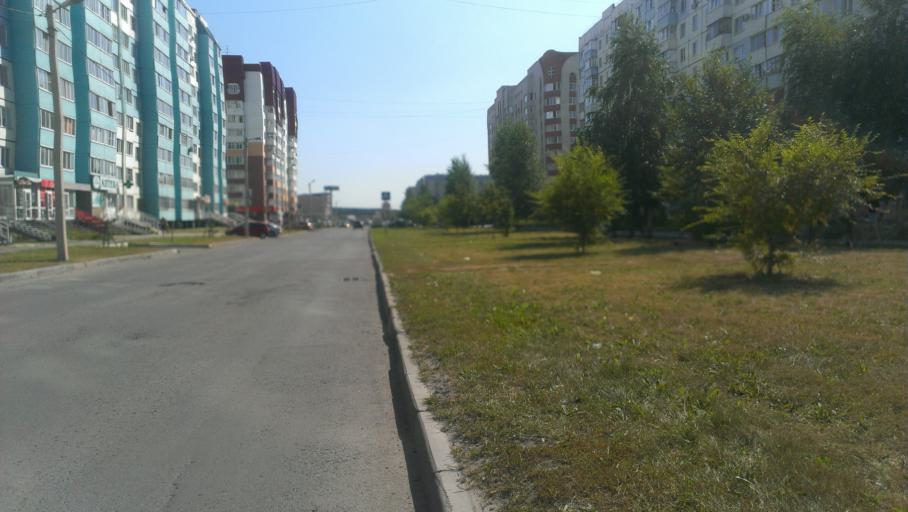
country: RU
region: Altai Krai
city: Novosilikatnyy
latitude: 53.3324
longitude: 83.6848
